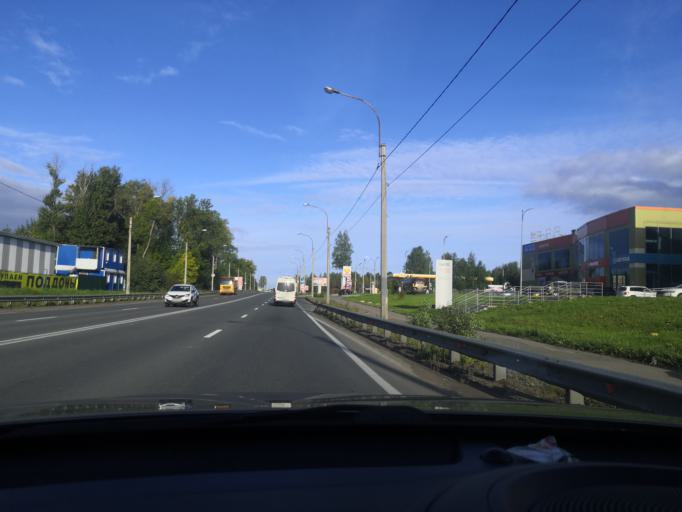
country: RU
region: St.-Petersburg
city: Pargolovo
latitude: 60.0730
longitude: 30.2826
